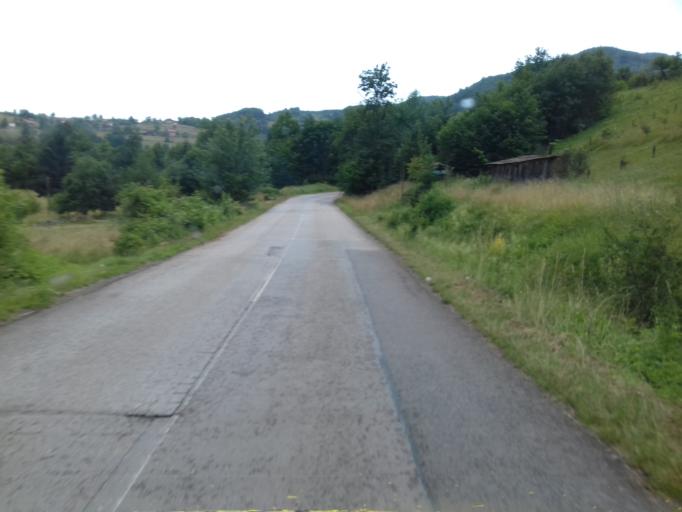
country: BA
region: Federation of Bosnia and Herzegovina
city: Visoko
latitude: 43.9574
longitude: 18.1677
